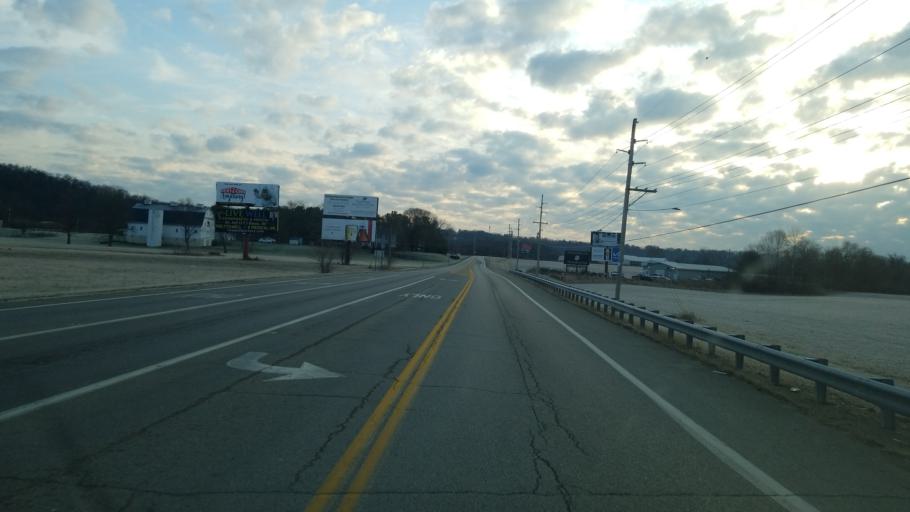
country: US
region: Ohio
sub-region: Ross County
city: North Fork Village
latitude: 39.3500
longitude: -83.0505
